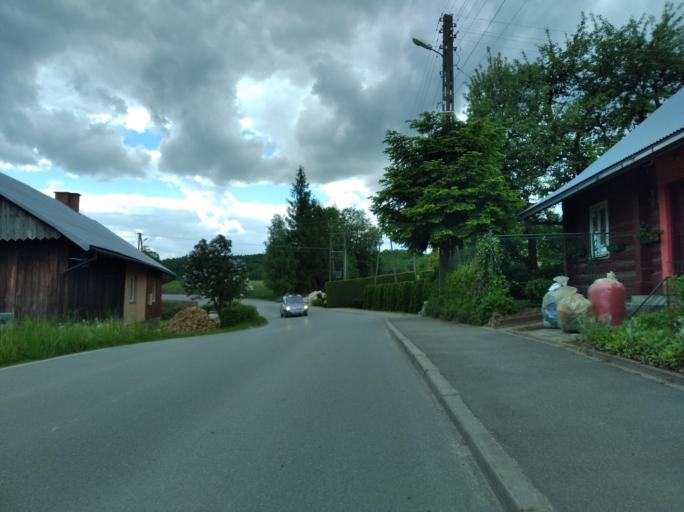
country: PL
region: Subcarpathian Voivodeship
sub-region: Powiat brzozowski
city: Jablonica Polska
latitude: 49.6963
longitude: 21.9039
